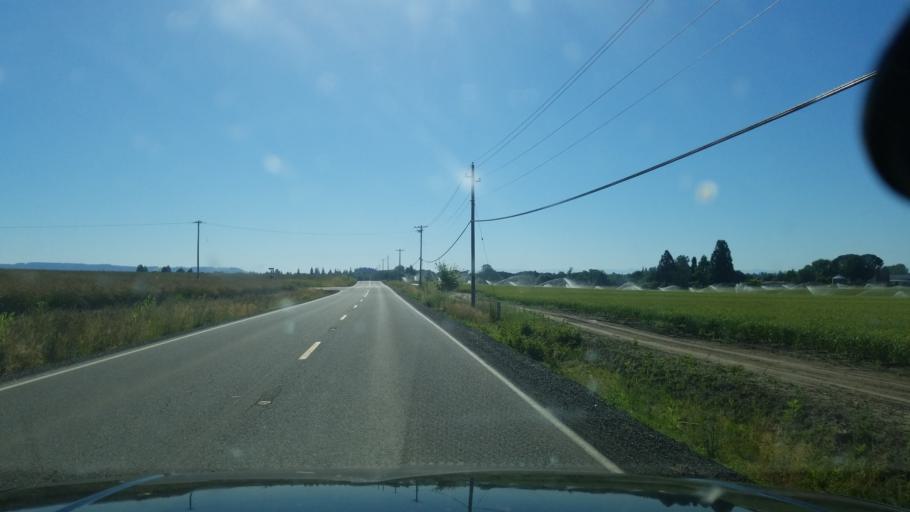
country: US
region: Oregon
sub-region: Yamhill County
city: McMinnville
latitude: 45.2305
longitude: -123.2491
